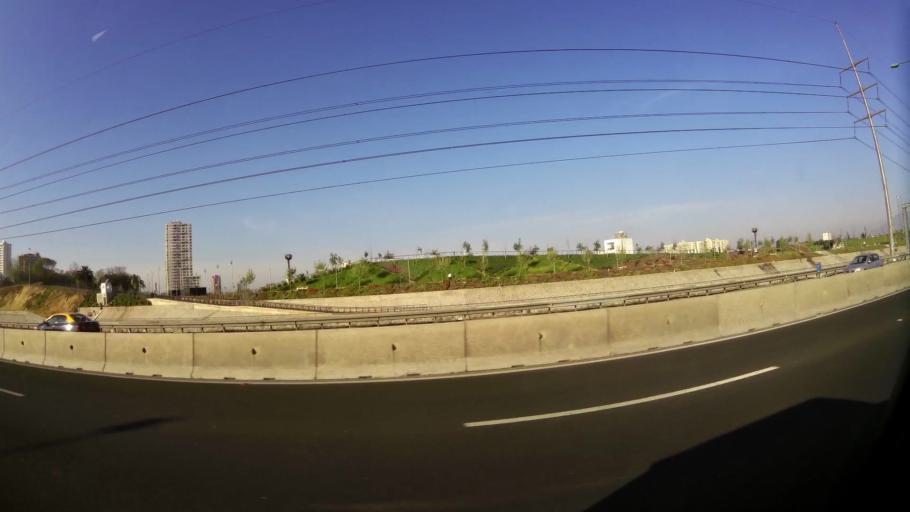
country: CL
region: Santiago Metropolitan
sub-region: Provincia de Santiago
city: Santiago
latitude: -33.4236
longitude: -70.6772
